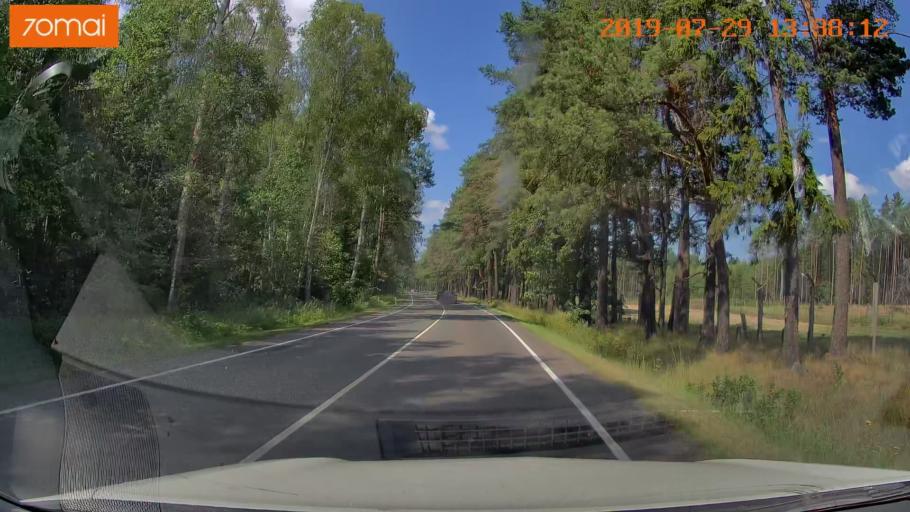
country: RU
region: Kaliningrad
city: Volochayevskoye
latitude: 54.7196
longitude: 20.1741
